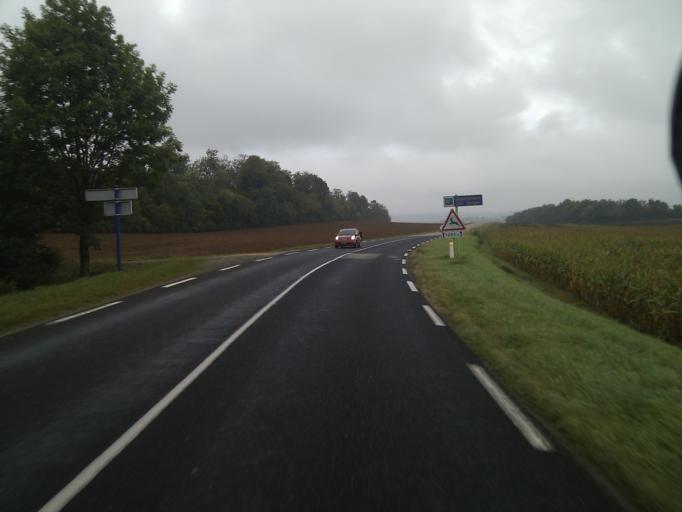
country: FR
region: Lorraine
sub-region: Departement de Meurthe-et-Moselle
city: Colombey-les-Belles
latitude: 48.4991
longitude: 5.8728
